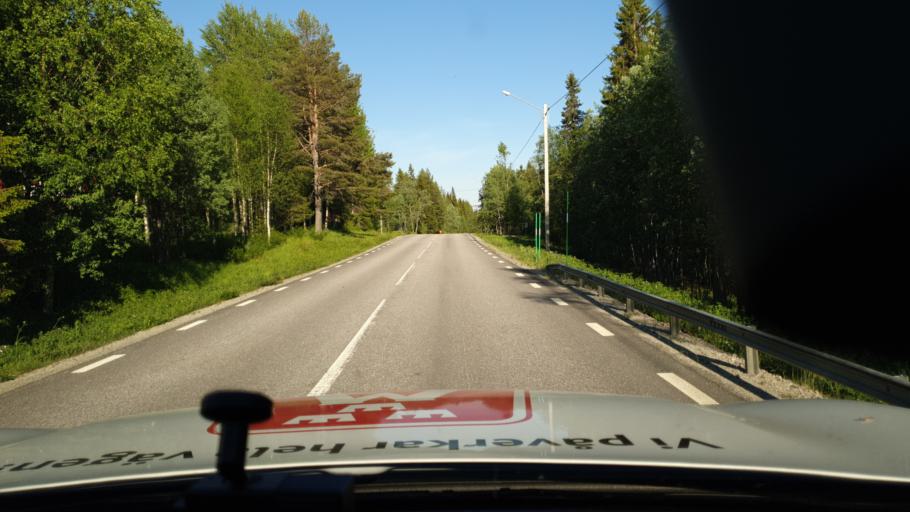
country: SE
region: Vaesterbotten
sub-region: Lycksele Kommun
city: Soderfors
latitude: 64.7136
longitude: 17.6896
